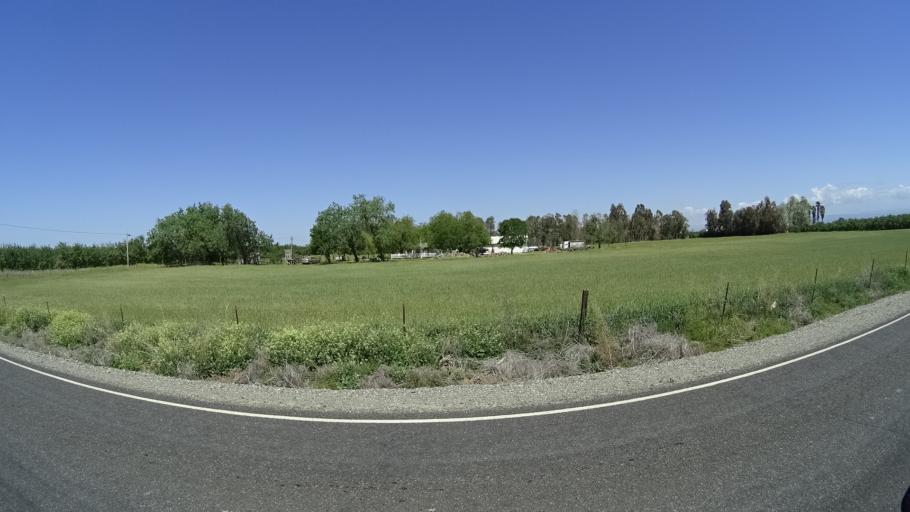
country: US
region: California
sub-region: Glenn County
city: Hamilton City
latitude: 39.7664
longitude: -122.0565
